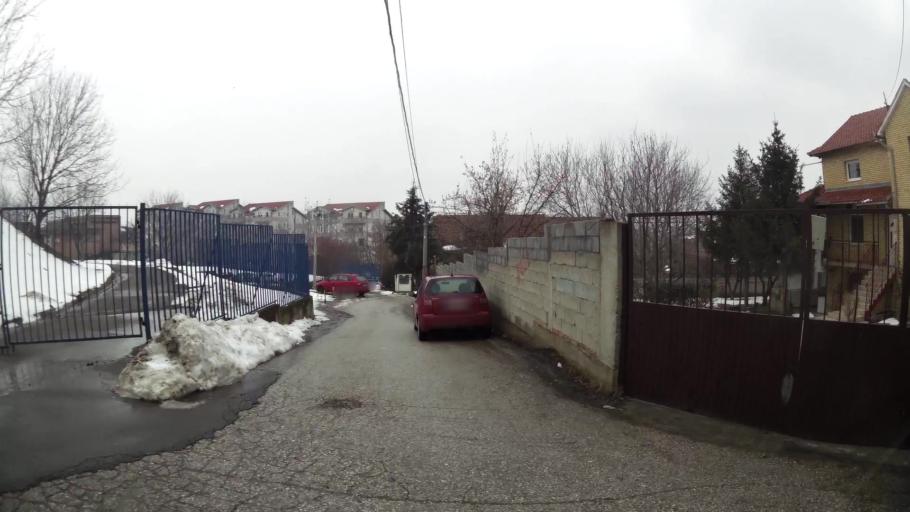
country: RS
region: Central Serbia
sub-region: Belgrade
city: Zvezdara
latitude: 44.7653
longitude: 20.5033
